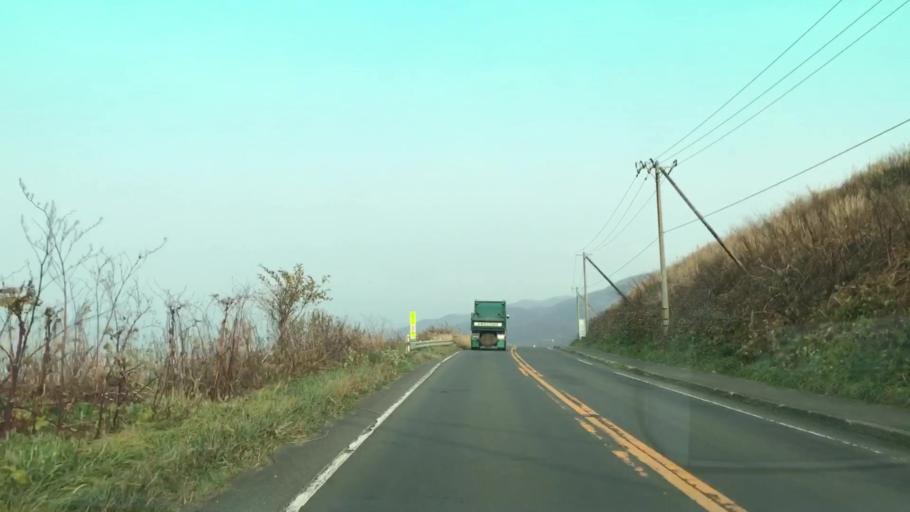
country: JP
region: Hokkaido
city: Ishikari
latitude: 43.4057
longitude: 141.4305
